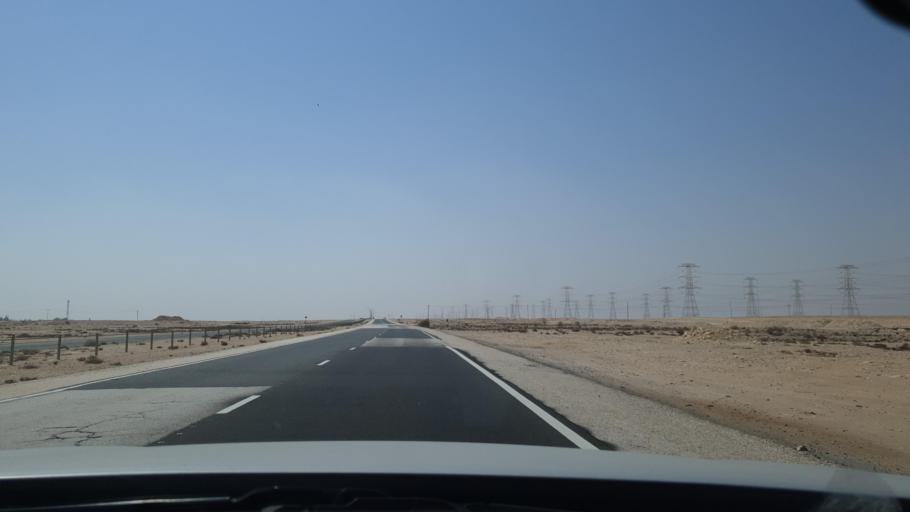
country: QA
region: Al Khawr
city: Al Khawr
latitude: 25.7411
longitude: 51.4616
